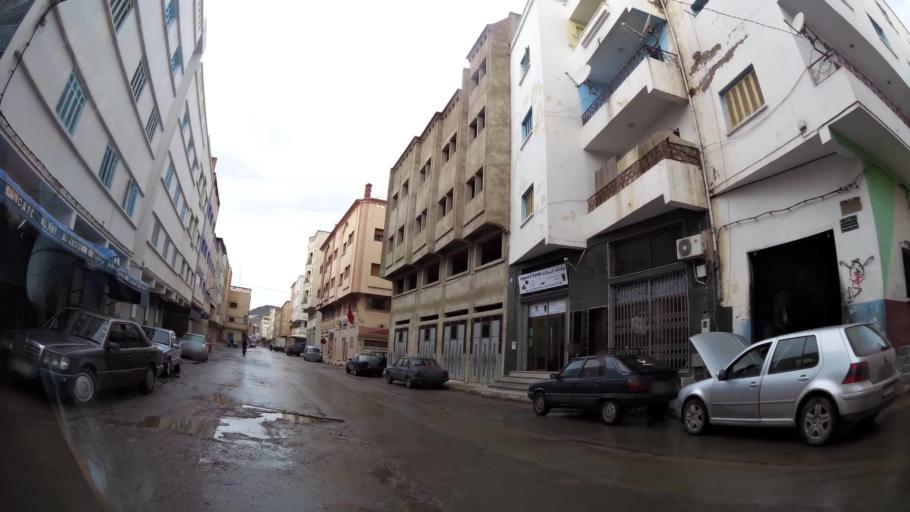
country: MA
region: Oriental
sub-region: Nador
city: Nador
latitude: 35.1544
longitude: -2.9995
